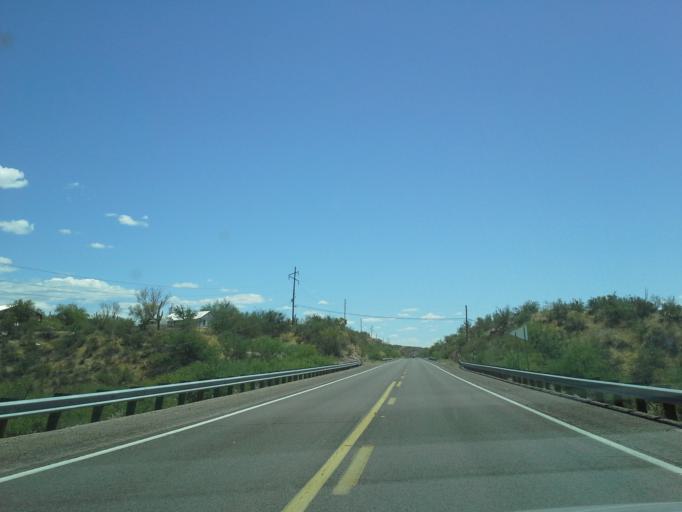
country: US
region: Arizona
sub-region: Pinal County
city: Mammoth
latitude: 32.9246
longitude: -110.7276
